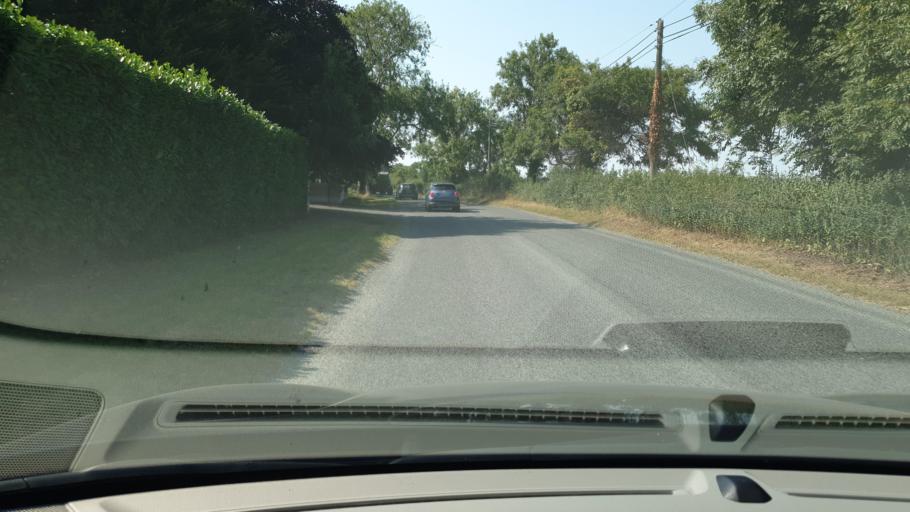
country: IE
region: Leinster
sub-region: An Mhi
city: Trim
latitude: 53.5711
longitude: -6.8241
